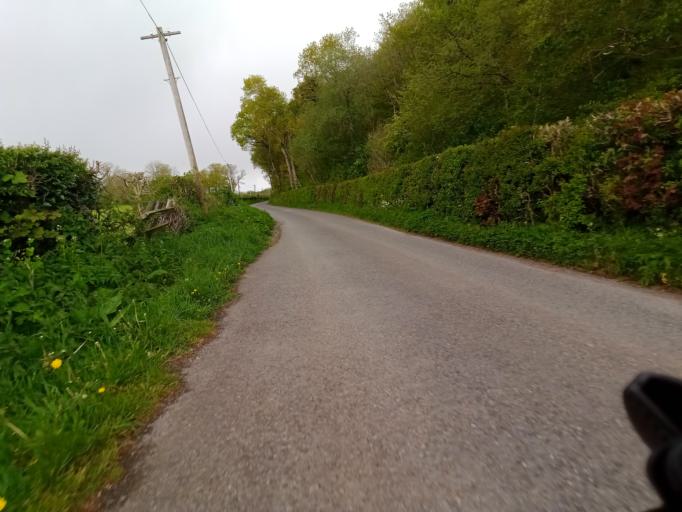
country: IE
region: Leinster
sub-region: Kilkenny
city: Kilkenny
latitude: 52.6847
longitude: -7.2679
